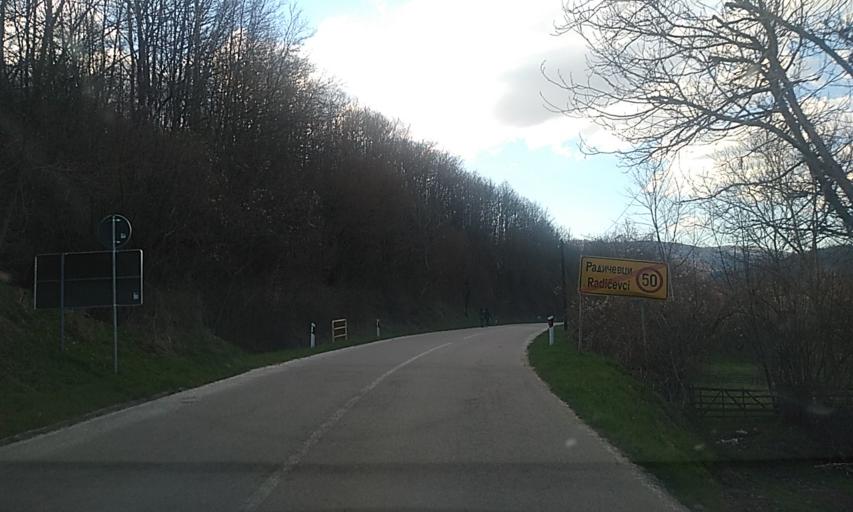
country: RS
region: Central Serbia
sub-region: Pcinjski Okrug
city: Bosilegrad
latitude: 42.4694
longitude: 22.4823
